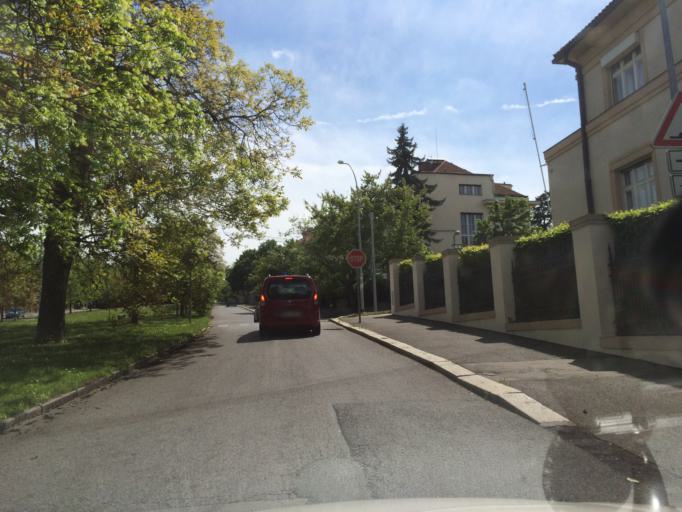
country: CZ
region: Praha
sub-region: Praha 1
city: Mala Strana
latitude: 50.0956
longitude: 14.3864
